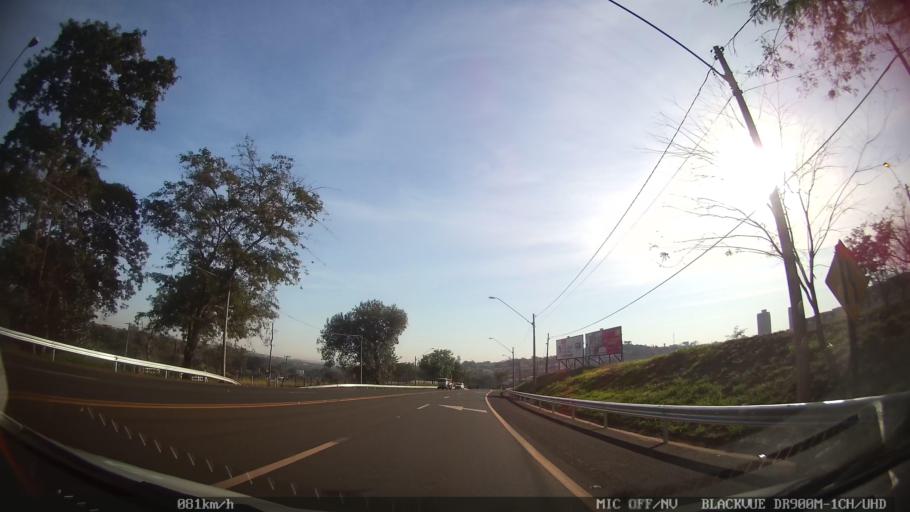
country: BR
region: Sao Paulo
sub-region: Ribeirao Preto
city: Ribeirao Preto
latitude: -21.2735
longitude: -47.8183
